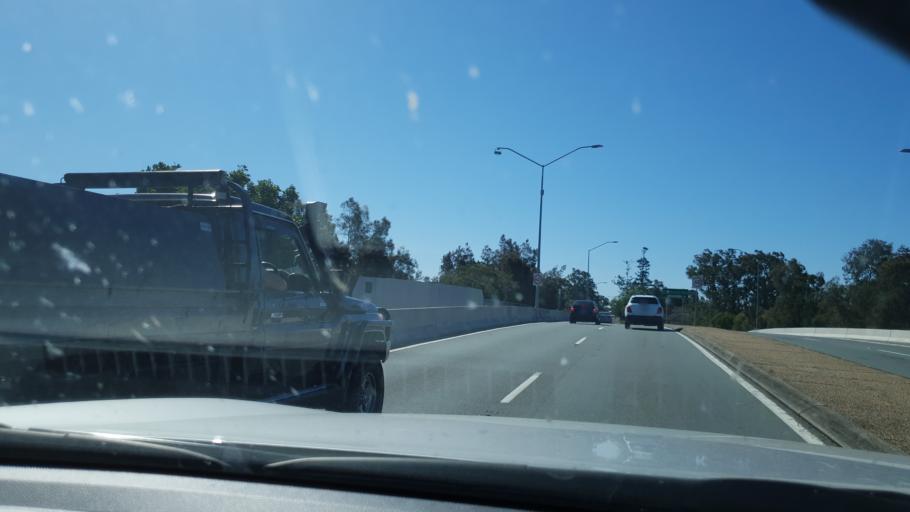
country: AU
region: Queensland
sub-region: Brisbane
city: Everton Park
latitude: -27.4202
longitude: 152.9914
